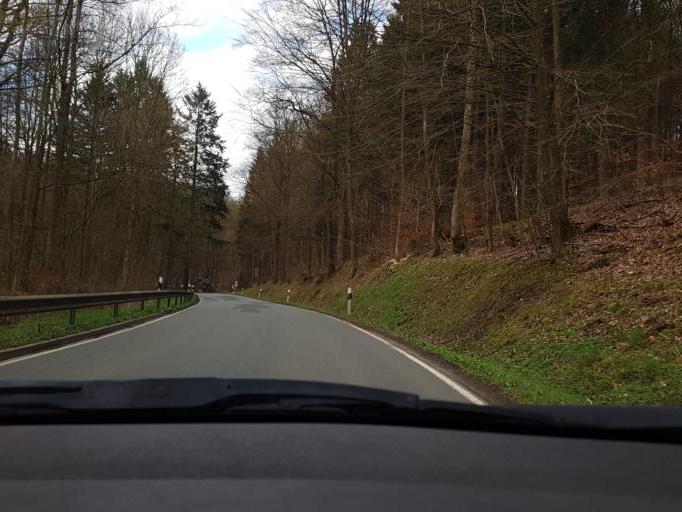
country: DE
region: Lower Saxony
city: Bodenfelde
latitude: 51.6853
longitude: 9.5289
